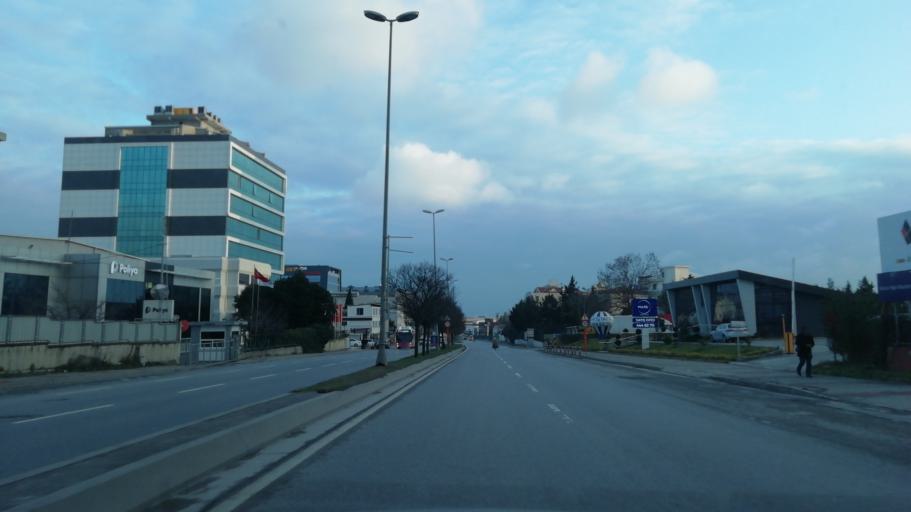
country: TR
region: Istanbul
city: Yakuplu
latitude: 40.9963
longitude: 28.7147
